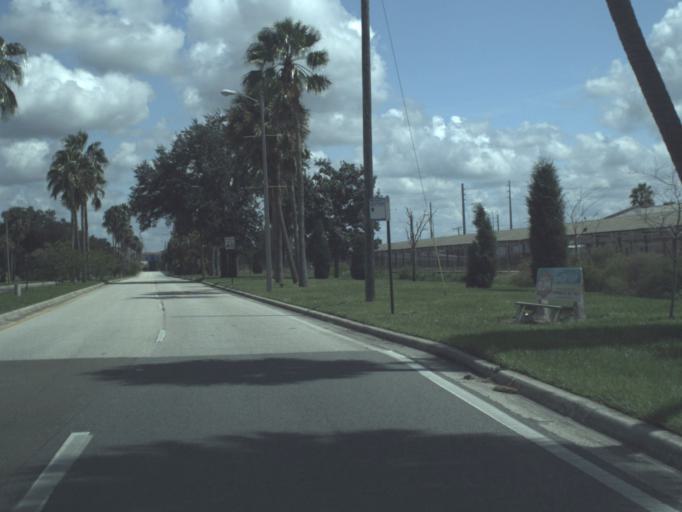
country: US
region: Florida
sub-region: Hillsborough County
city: Tampa
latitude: 27.9534
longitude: -82.4510
